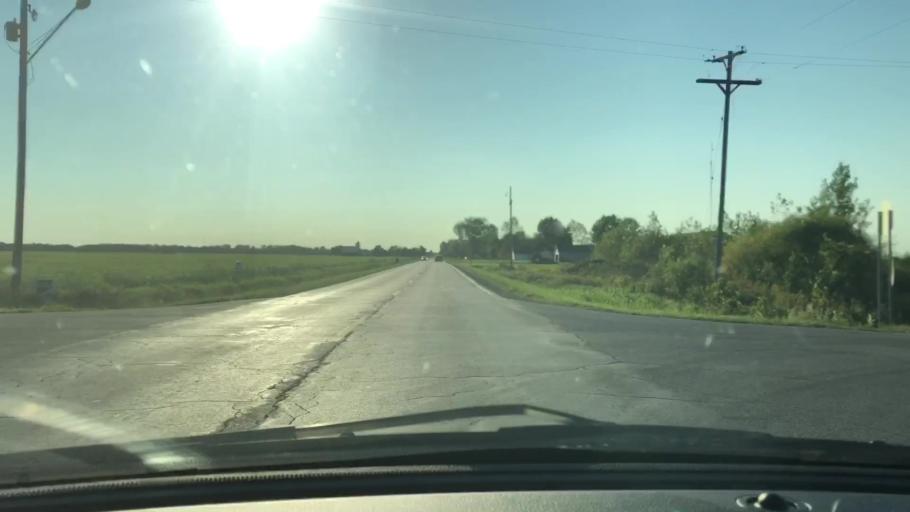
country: US
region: Michigan
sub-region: Bay County
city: Auburn
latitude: 43.6401
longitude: -84.1082
